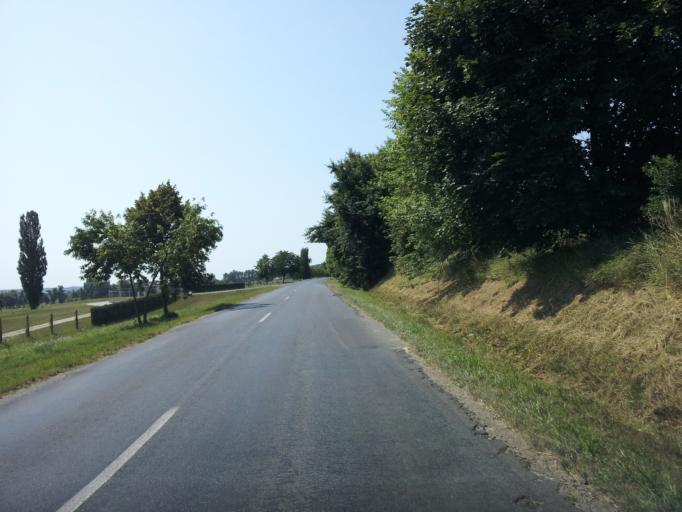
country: HU
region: Zala
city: Heviz
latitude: 46.8233
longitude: 17.0932
